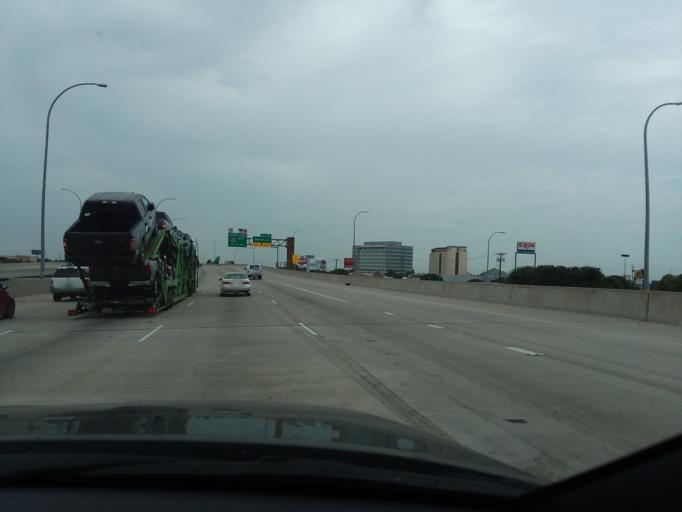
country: US
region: Texas
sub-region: Dallas County
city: Addison
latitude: 32.9258
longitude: -96.8367
